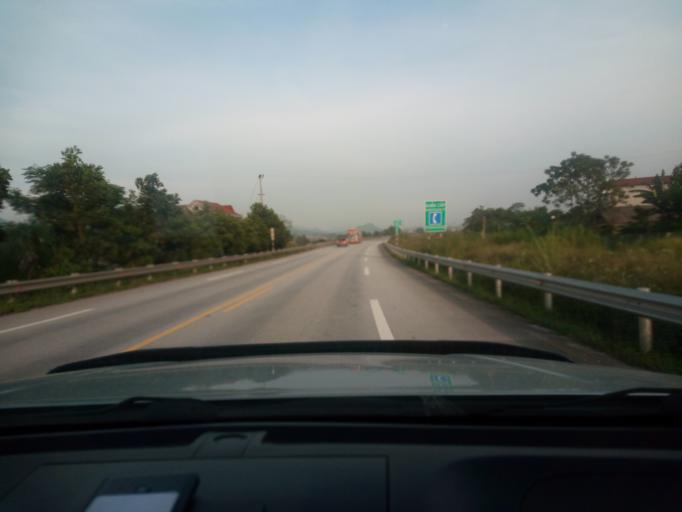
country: VN
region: Yen Bai
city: Co Phuc
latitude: 21.8856
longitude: 104.6649
